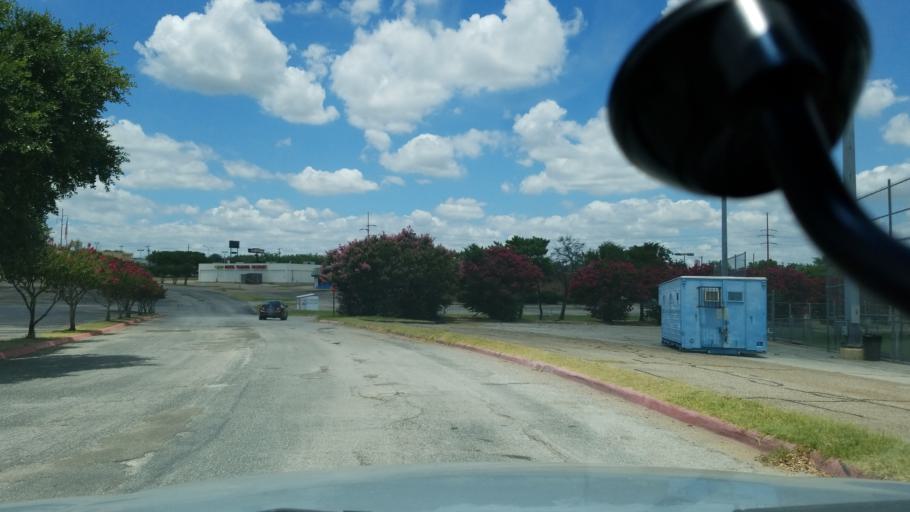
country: US
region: Texas
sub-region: Dallas County
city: Duncanville
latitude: 32.6608
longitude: -96.8745
